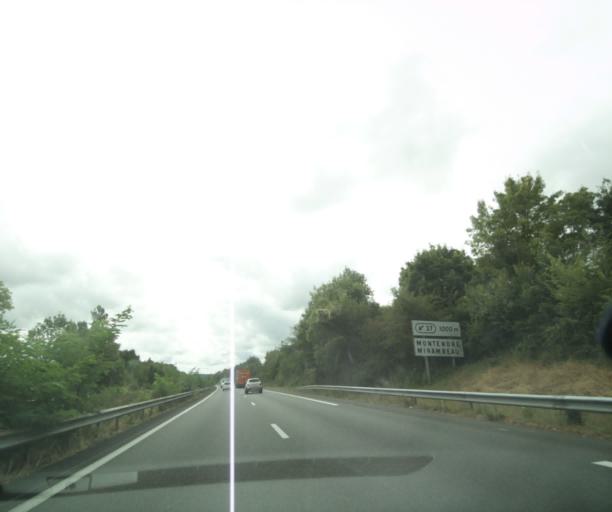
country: FR
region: Poitou-Charentes
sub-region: Departement de la Charente-Maritime
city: Mirambeau
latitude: 45.3798
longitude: -0.6005
